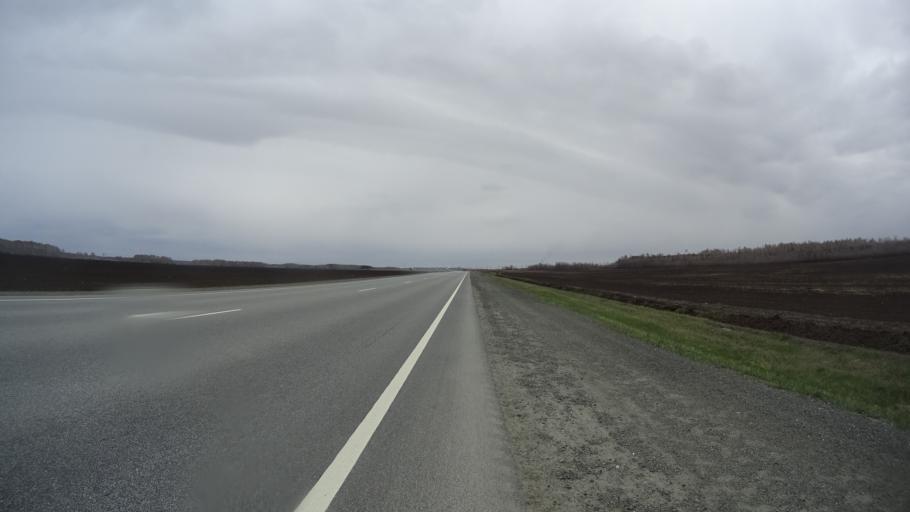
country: RU
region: Chelyabinsk
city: Krasnogorskiy
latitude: 54.5714
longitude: 61.2906
